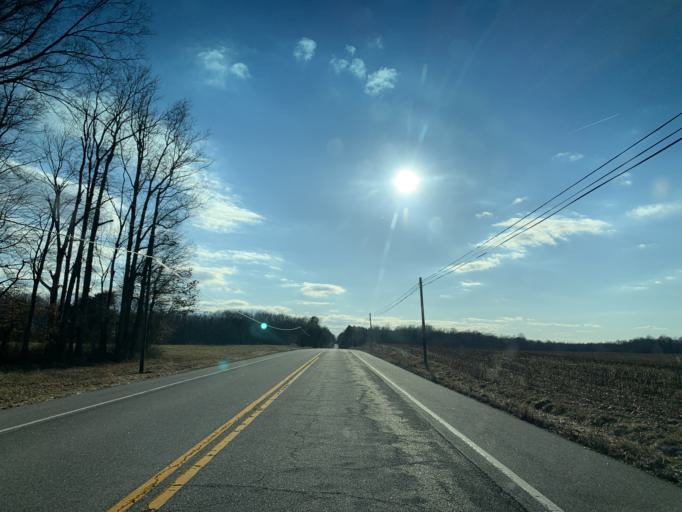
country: US
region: Maryland
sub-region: Queen Anne's County
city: Kingstown
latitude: 39.1582
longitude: -75.9500
